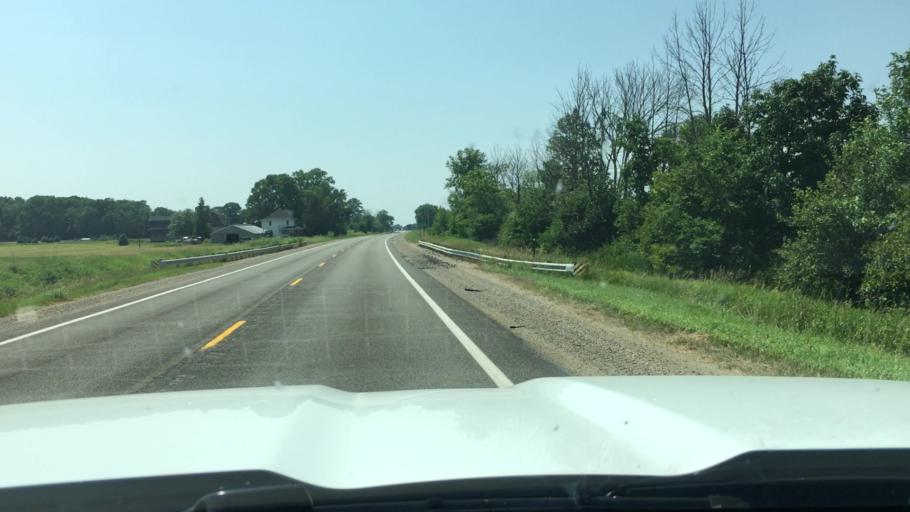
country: US
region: Michigan
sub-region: Gratiot County
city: Ithaca
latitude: 43.1757
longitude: -84.4822
